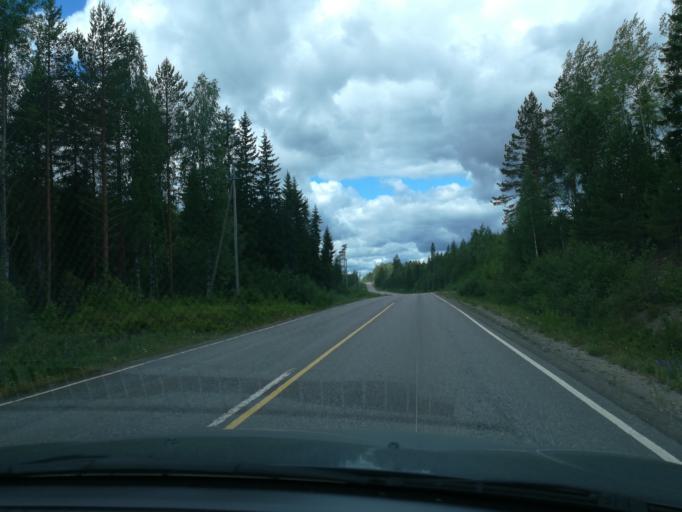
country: FI
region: Southern Savonia
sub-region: Mikkeli
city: Maentyharju
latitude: 61.3641
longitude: 26.9987
